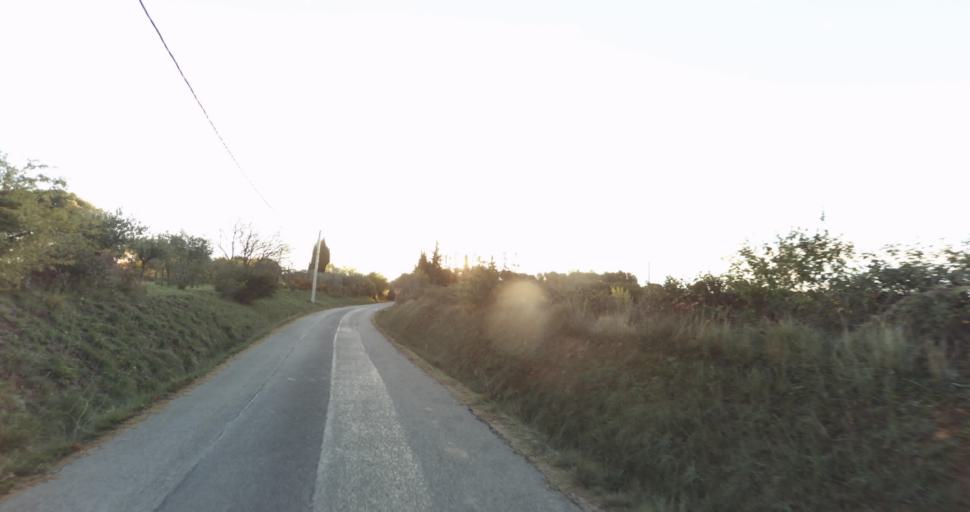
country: FR
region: Provence-Alpes-Cote d'Azur
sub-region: Departement des Bouches-du-Rhone
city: Venelles
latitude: 43.5774
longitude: 5.4818
